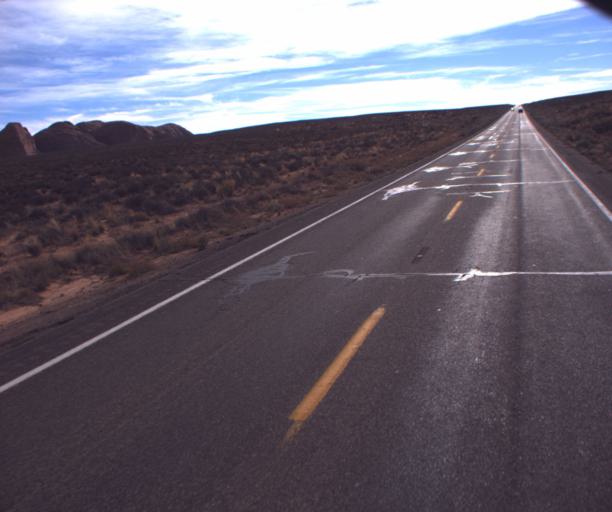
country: US
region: Arizona
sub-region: Coconino County
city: LeChee
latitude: 36.8407
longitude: -111.3253
